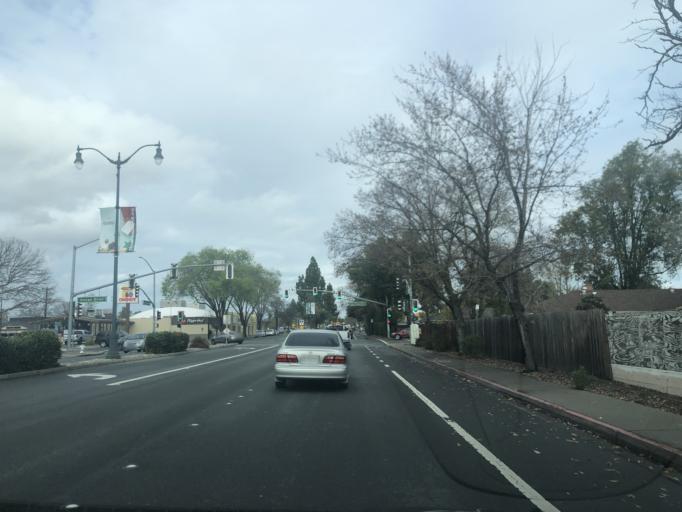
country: US
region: California
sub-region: Contra Costa County
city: Pleasant Hill
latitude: 37.9511
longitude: -122.0601
